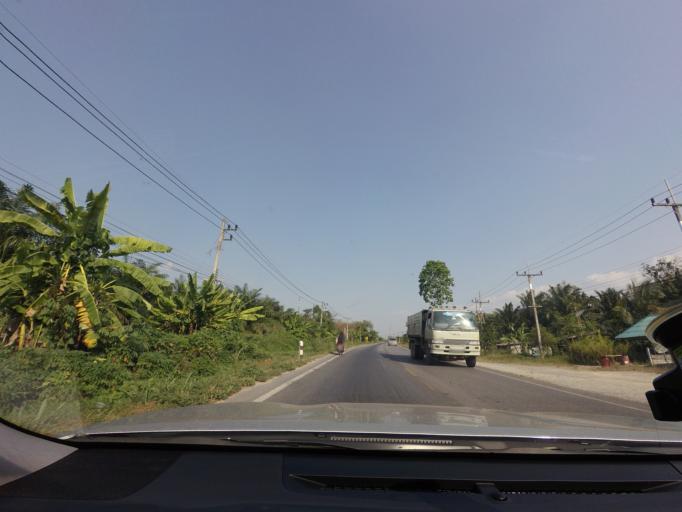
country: TH
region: Surat Thani
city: Phrasaeng
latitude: 8.5607
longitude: 99.1517
